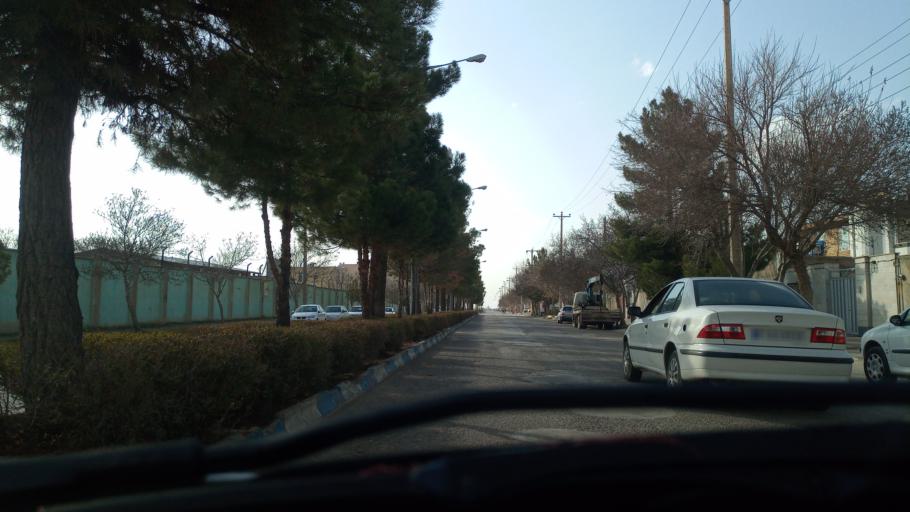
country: IR
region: Razavi Khorasan
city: Quchan
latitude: 37.1012
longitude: 58.4982
